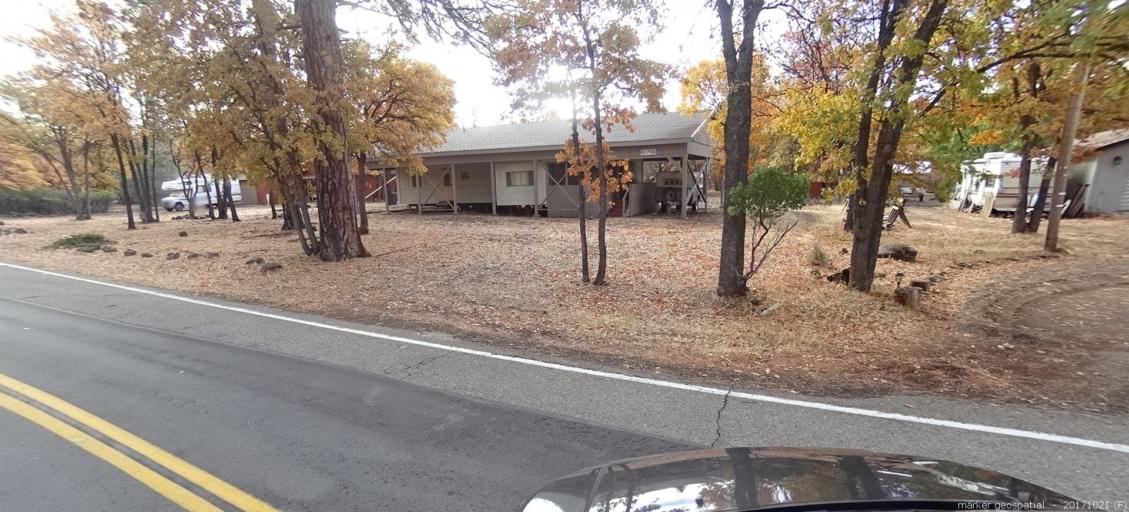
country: US
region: California
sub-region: Shasta County
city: Burney
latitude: 40.9199
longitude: -121.5602
